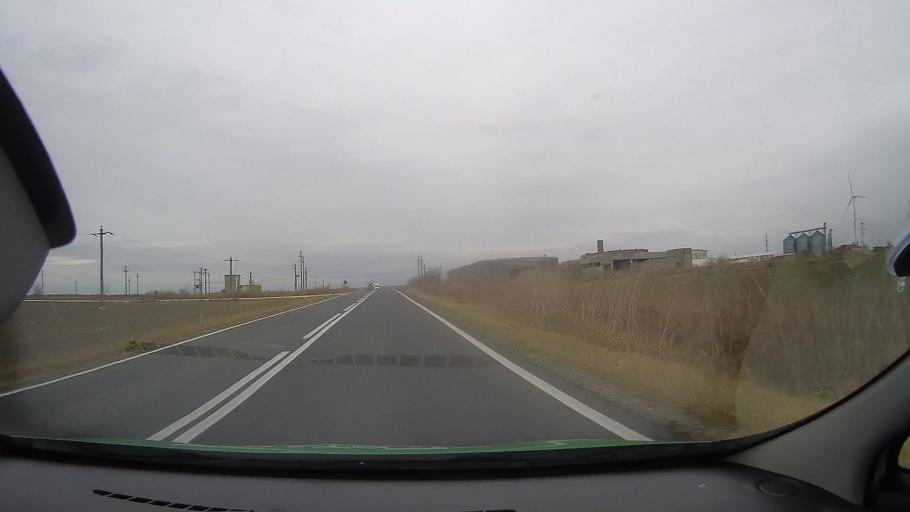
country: RO
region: Constanta
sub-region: Comuna Nicolae Balcescu
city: Dorobantu
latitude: 44.4230
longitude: 28.3107
